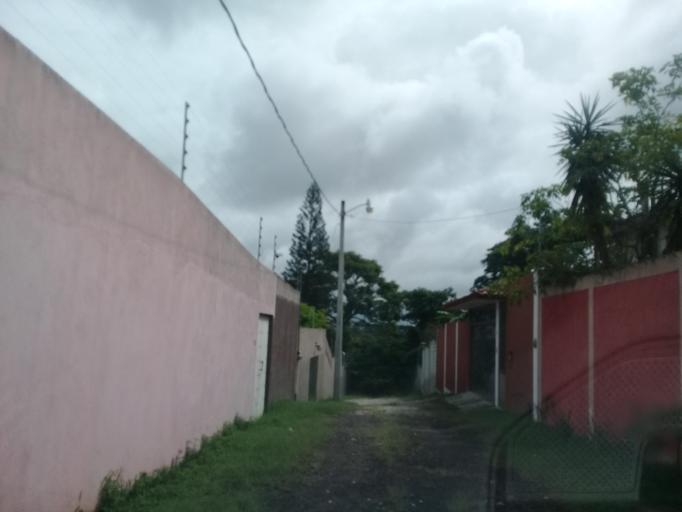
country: MX
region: Veracruz
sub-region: Emiliano Zapata
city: Jacarandas
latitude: 19.4833
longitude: -96.8539
